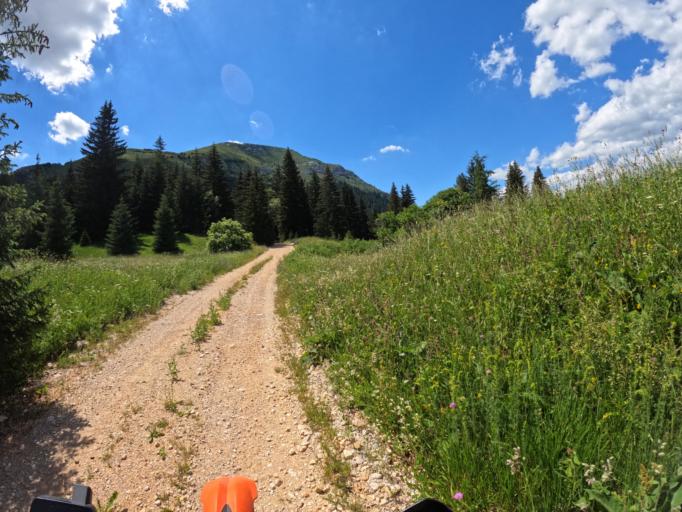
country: BA
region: Federation of Bosnia and Herzegovina
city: Livno
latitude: 43.9310
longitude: 17.1122
